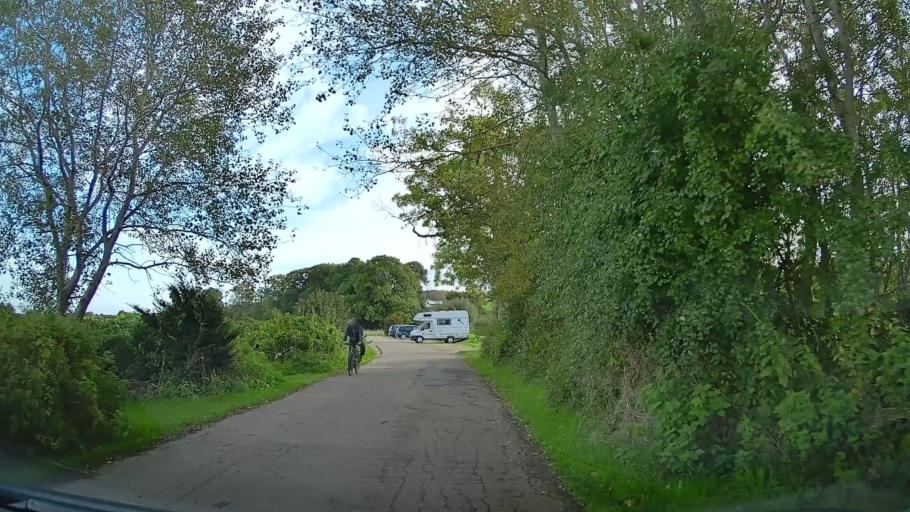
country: DE
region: Schleswig-Holstein
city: Ringsberg
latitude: 54.8305
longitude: 9.6040
